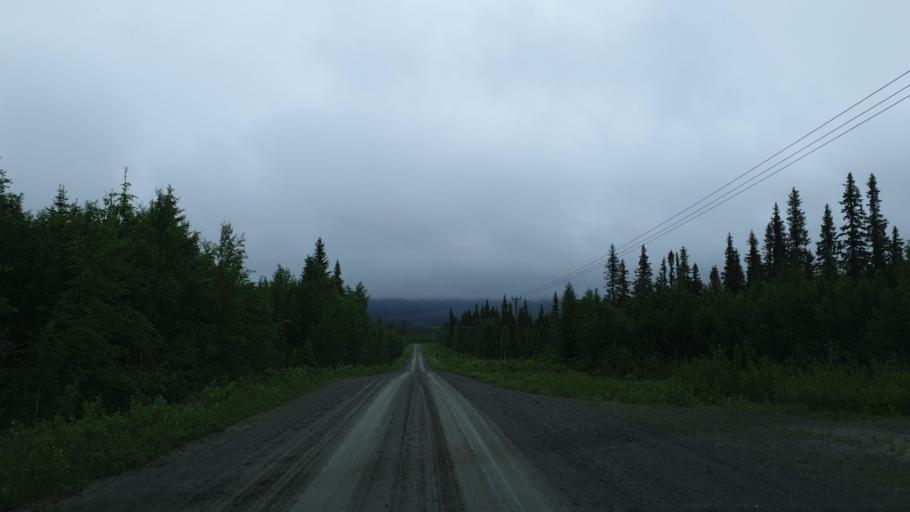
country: SE
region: Vaesterbotten
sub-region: Vilhelmina Kommun
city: Sjoberg
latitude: 65.3109
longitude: 15.9955
